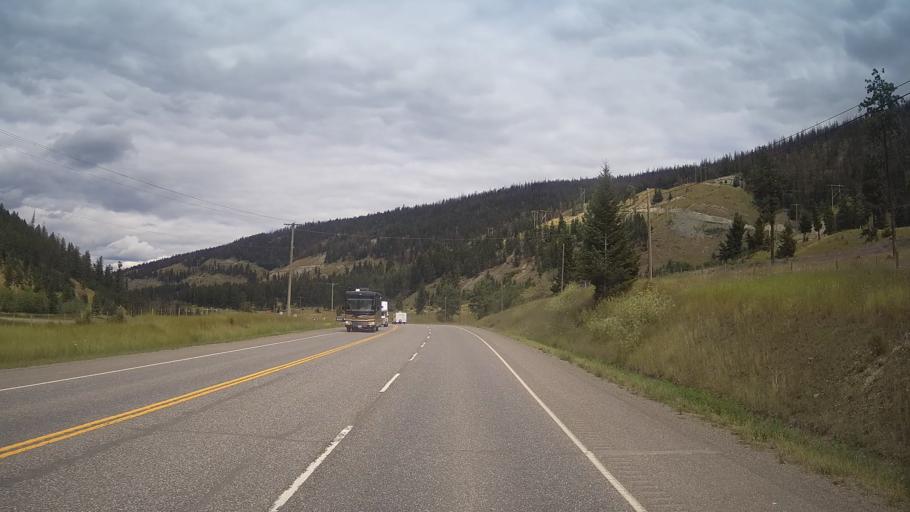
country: CA
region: British Columbia
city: Cache Creek
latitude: 51.0470
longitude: -121.5496
